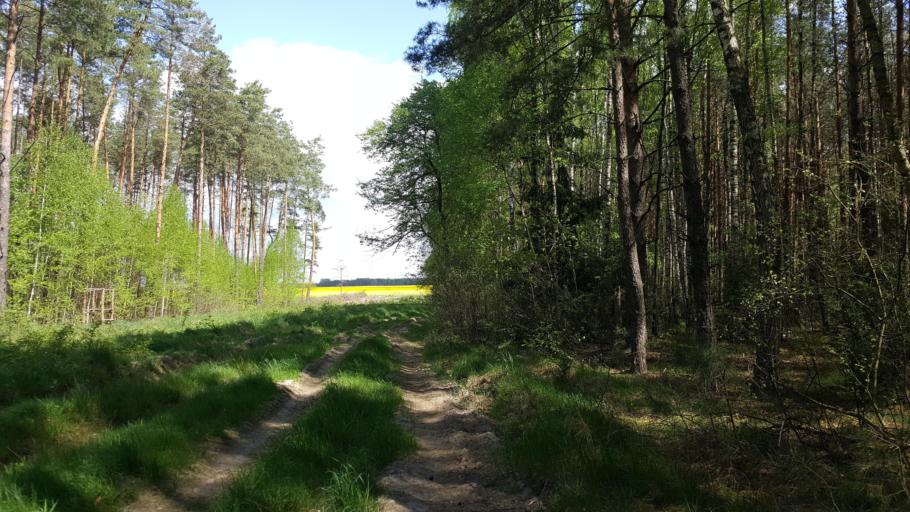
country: BY
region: Brest
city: Kamyanyets
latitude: 52.3867
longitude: 23.9334
